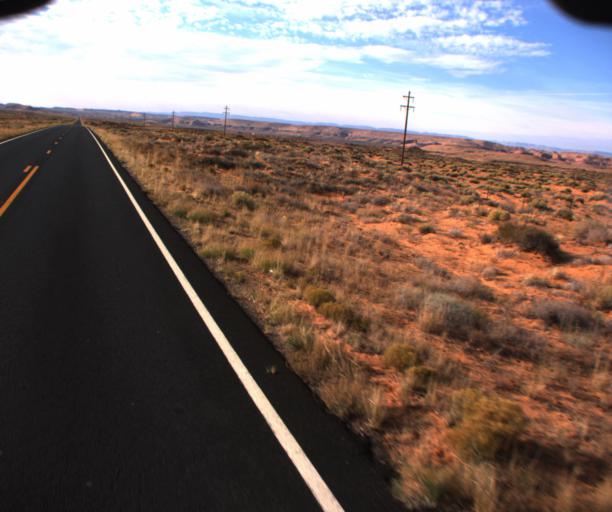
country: US
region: Arizona
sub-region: Apache County
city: Many Farms
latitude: 36.8262
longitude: -109.6444
